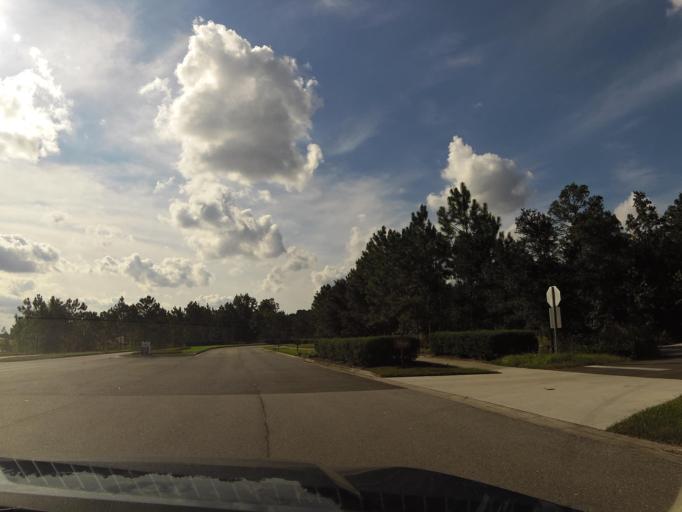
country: US
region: Florida
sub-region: Saint Johns County
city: Saint Augustine
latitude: 29.9320
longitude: -81.4979
